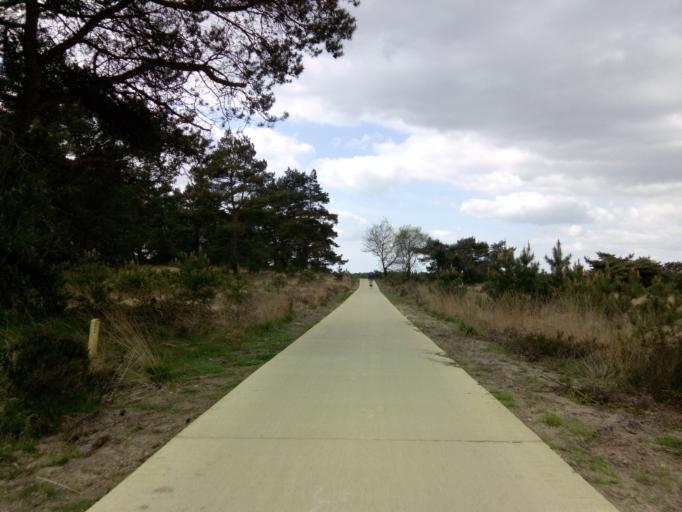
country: NL
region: Gelderland
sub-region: Gemeente Ede
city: Wekerom
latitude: 52.0651
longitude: 5.7091
